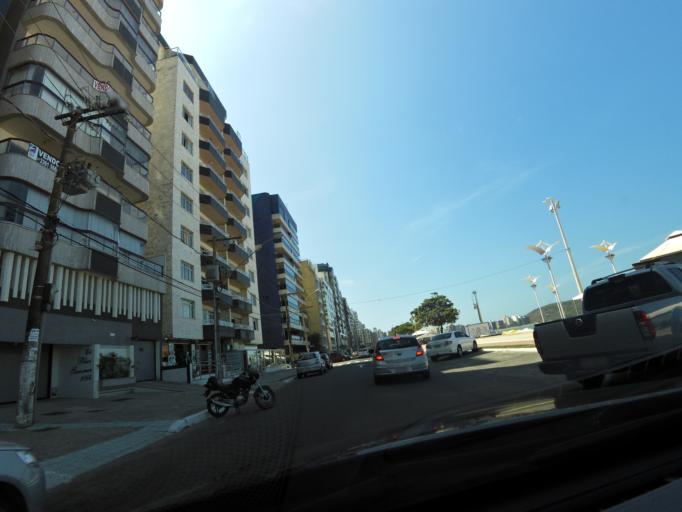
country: BR
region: Espirito Santo
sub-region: Guarapari
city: Guarapari
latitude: -20.6553
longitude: -40.4896
